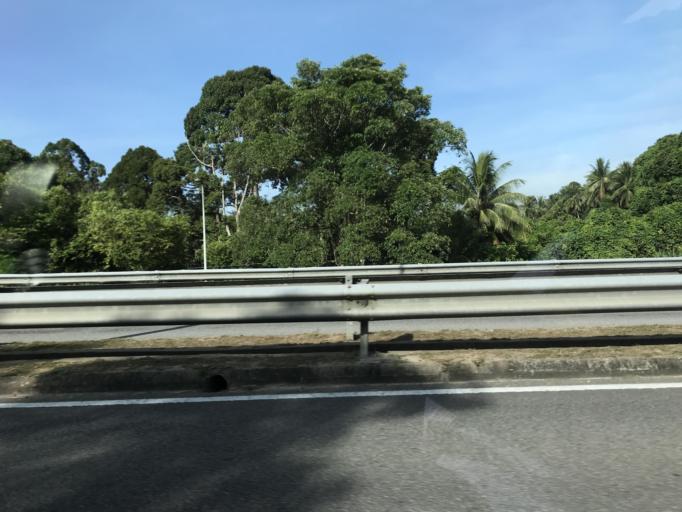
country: MY
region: Kelantan
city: Pasir Mas
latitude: 6.0603
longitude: 102.2098
